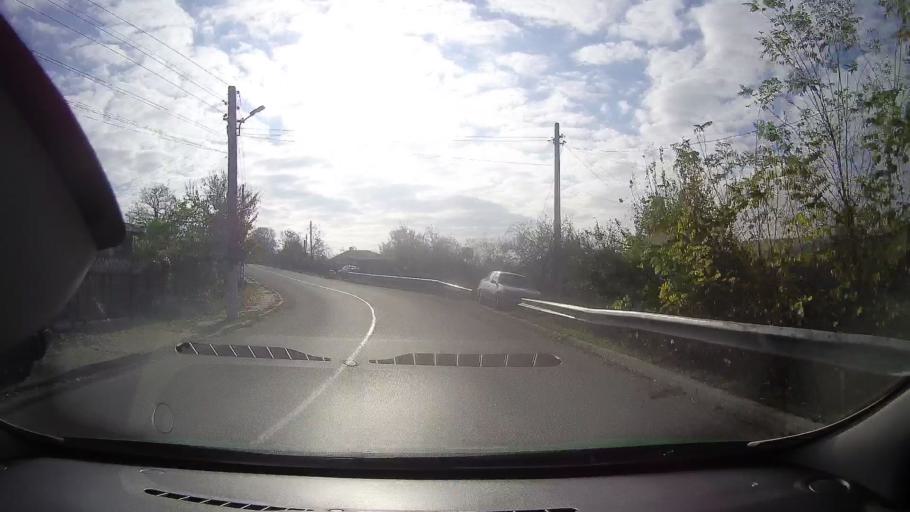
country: RO
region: Tulcea
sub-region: Comuna Bestepe
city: Bestepe
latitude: 45.0858
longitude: 29.0192
